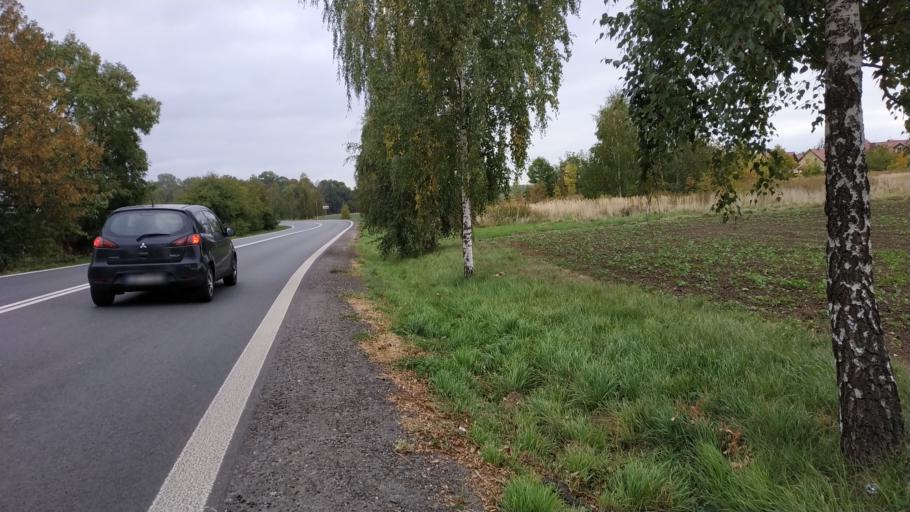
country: PL
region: Lower Silesian Voivodeship
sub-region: Powiat wroclawski
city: Tyniec Maly
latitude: 51.0237
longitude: 16.9257
